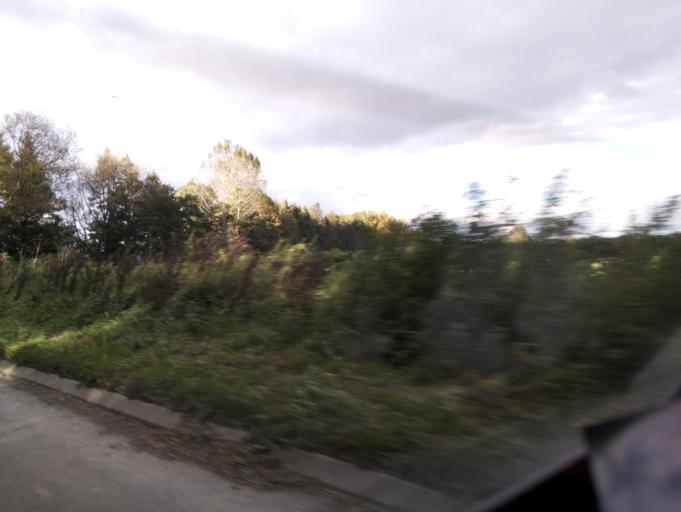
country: GB
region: England
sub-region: Herefordshire
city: Kinnersley
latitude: 52.1160
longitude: -2.9757
